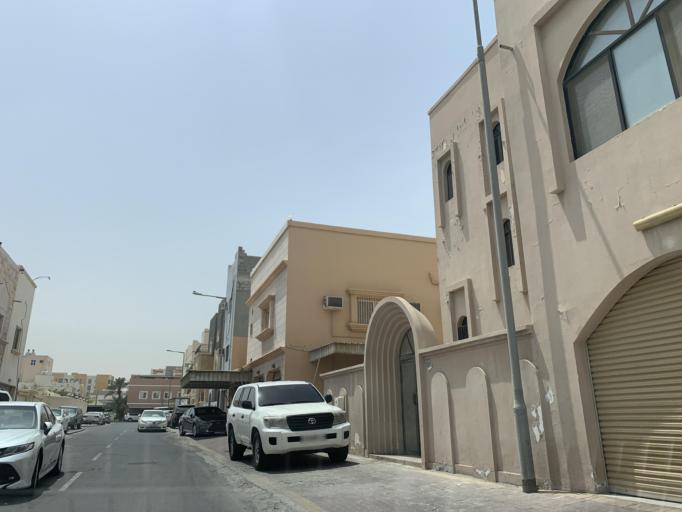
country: BH
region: Northern
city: Madinat `Isa
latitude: 26.1738
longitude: 50.5516
